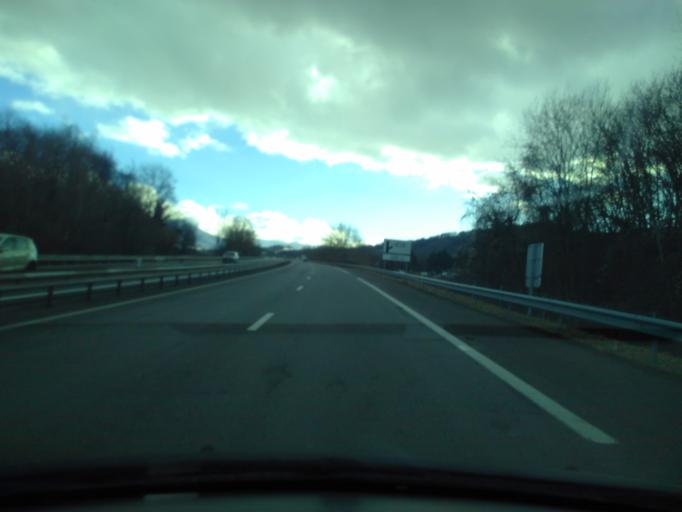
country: FR
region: Rhone-Alpes
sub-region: Departement de la Haute-Savoie
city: Cornier
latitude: 46.0934
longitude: 6.2899
